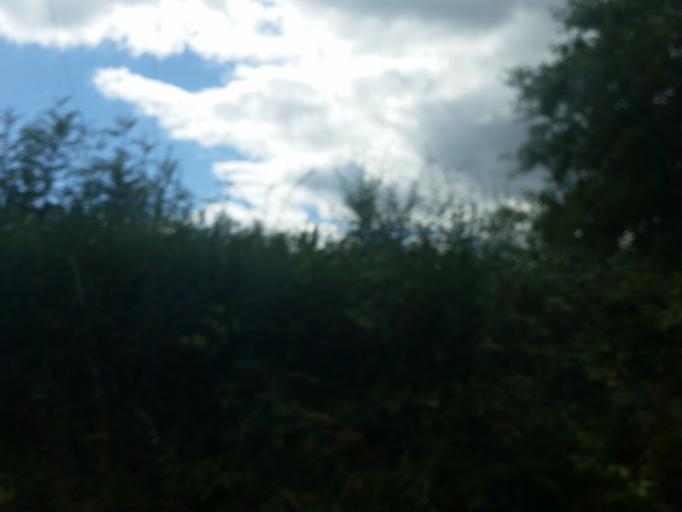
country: IE
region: Munster
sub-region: Waterford
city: Portlaw
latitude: 52.2125
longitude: -7.4304
